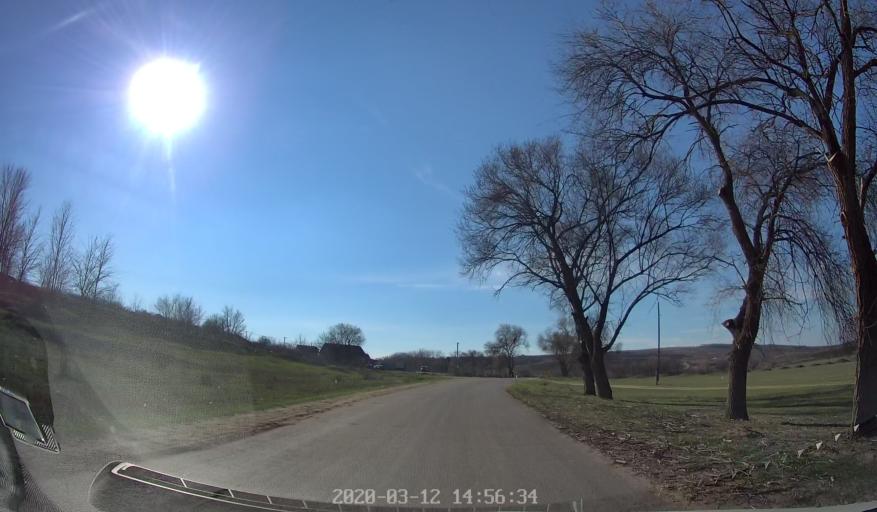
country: MD
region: Telenesti
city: Cocieri
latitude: 47.2250
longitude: 29.0475
